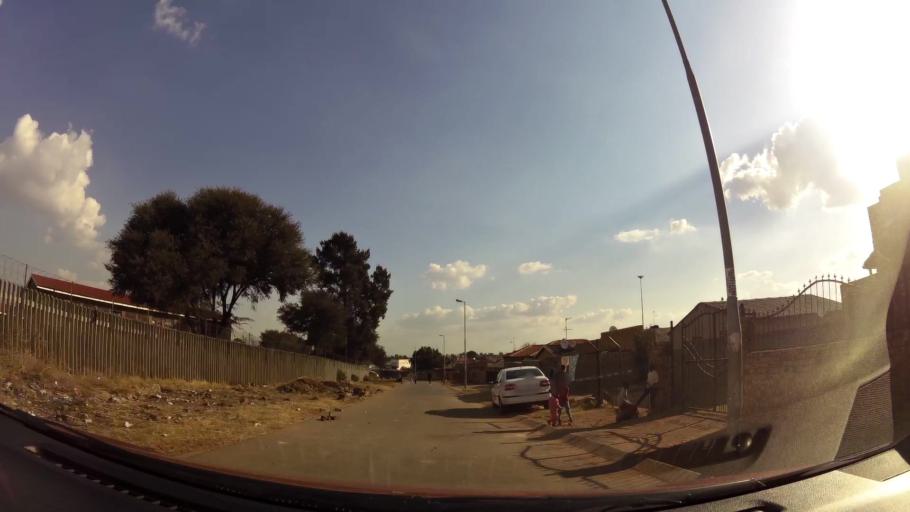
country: ZA
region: Gauteng
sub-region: City of Johannesburg Metropolitan Municipality
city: Soweto
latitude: -26.2326
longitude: 27.8678
